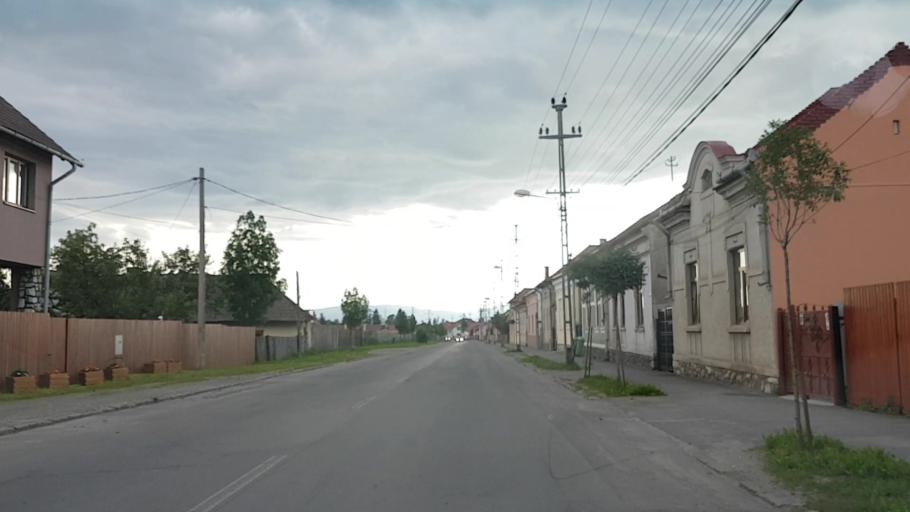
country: RO
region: Harghita
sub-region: Municipiul Gheorgheni
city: Gheorgheni
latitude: 46.7163
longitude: 25.5826
